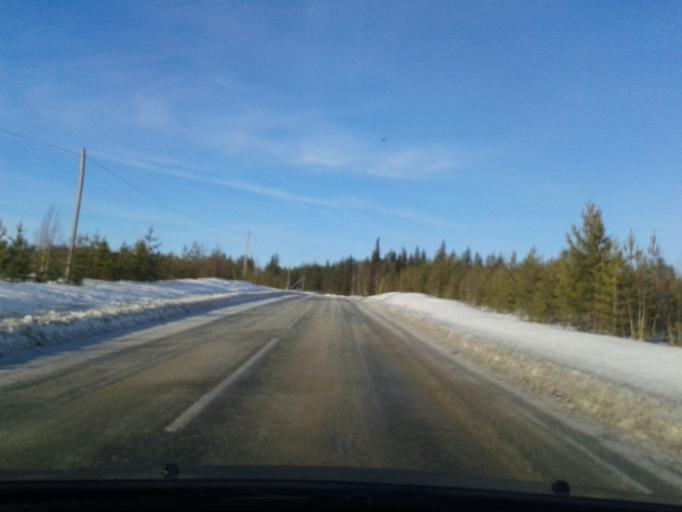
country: SE
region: Vaesternorrland
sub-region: OErnskoeldsviks Kommun
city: Bredbyn
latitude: 63.7277
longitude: 17.7476
